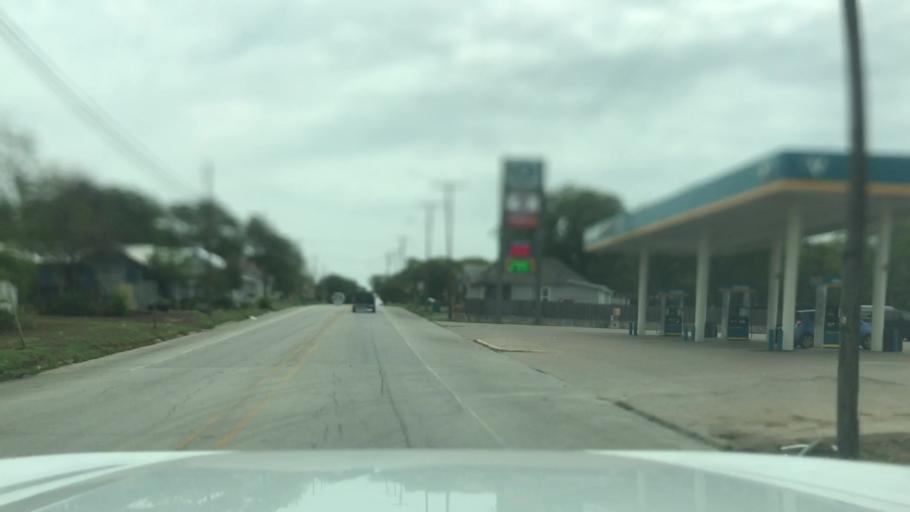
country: US
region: Texas
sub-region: Erath County
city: Dublin
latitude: 32.0841
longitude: -98.3381
